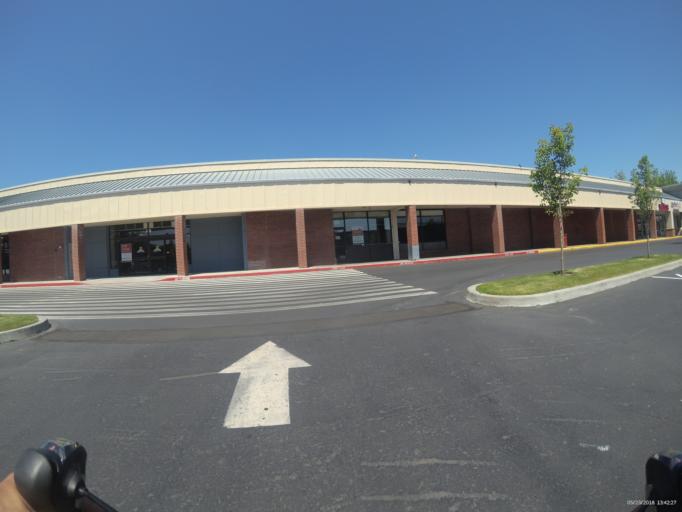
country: US
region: Washington
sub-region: Pierce County
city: Lakewood
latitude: 47.1647
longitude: -122.5187
